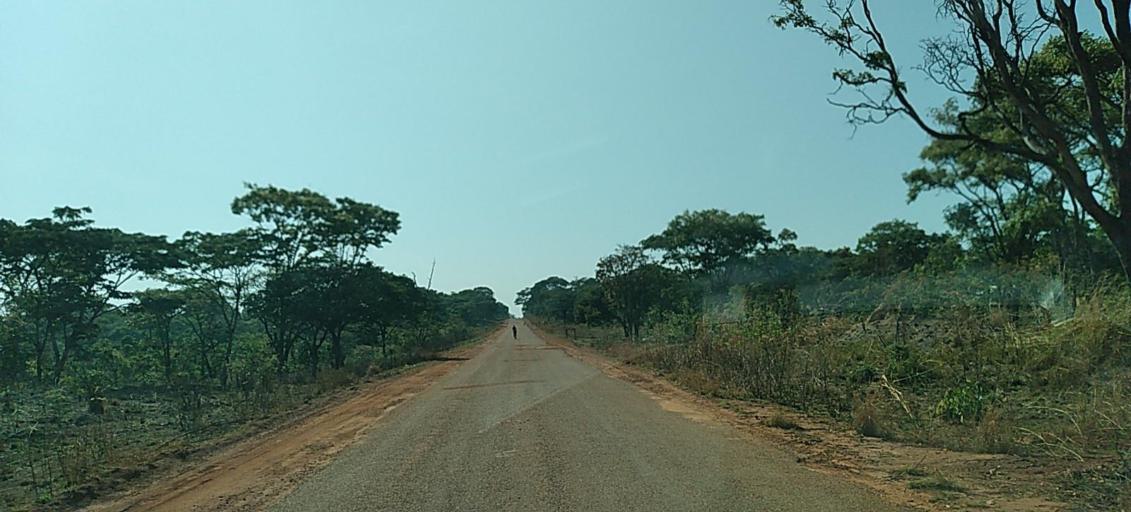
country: ZM
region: North-Western
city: Mwinilunga
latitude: -11.9028
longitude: 25.2827
